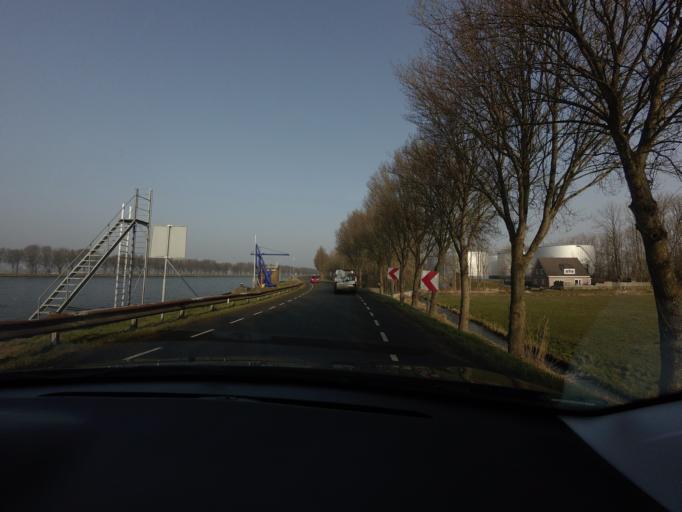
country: NL
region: North Holland
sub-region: Gemeente Amsterdam
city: Driemond
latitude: 52.2768
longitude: 5.0232
